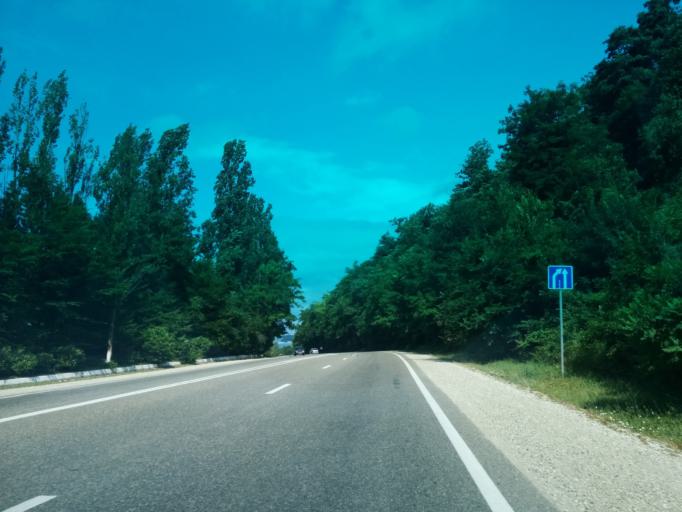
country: RU
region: Krasnodarskiy
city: Nebug
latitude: 44.1530
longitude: 39.0123
